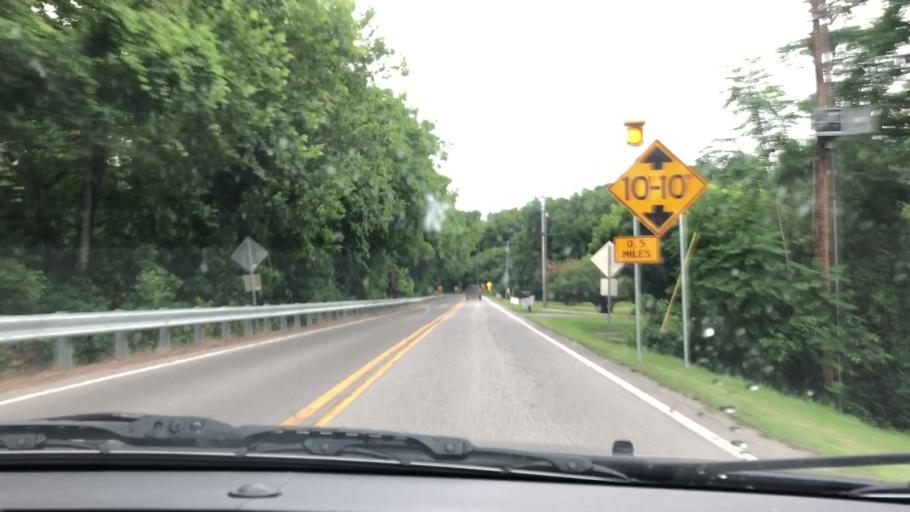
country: US
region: Tennessee
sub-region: Maury County
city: Columbia
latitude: 35.6732
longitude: -87.0075
